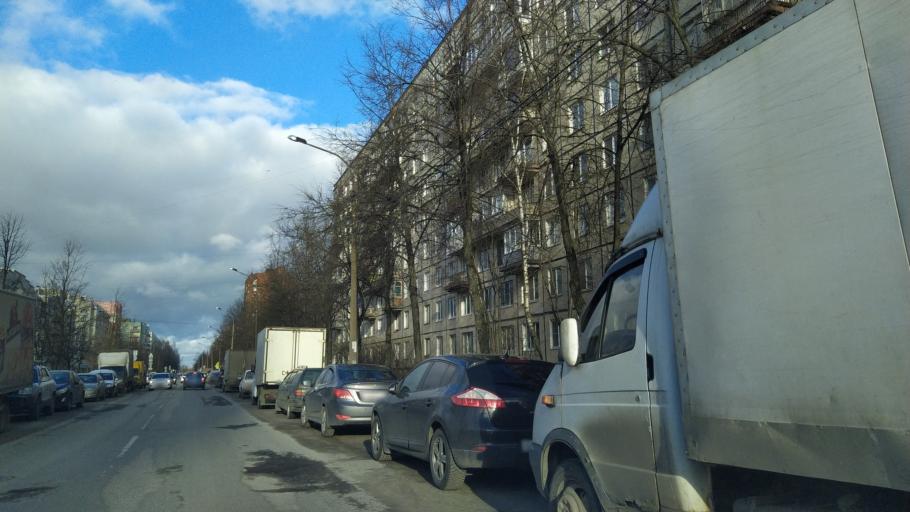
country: RU
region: Leningrad
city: Parnas
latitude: 60.0473
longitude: 30.3675
